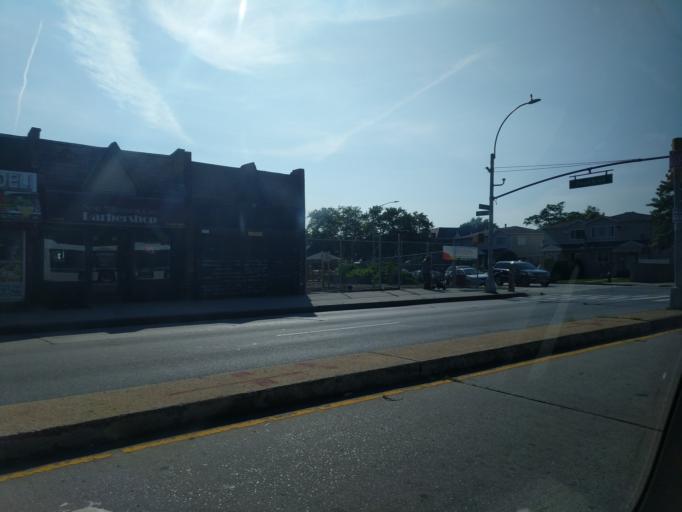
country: US
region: New York
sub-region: Queens County
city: Jamaica
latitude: 40.6868
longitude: -73.7746
